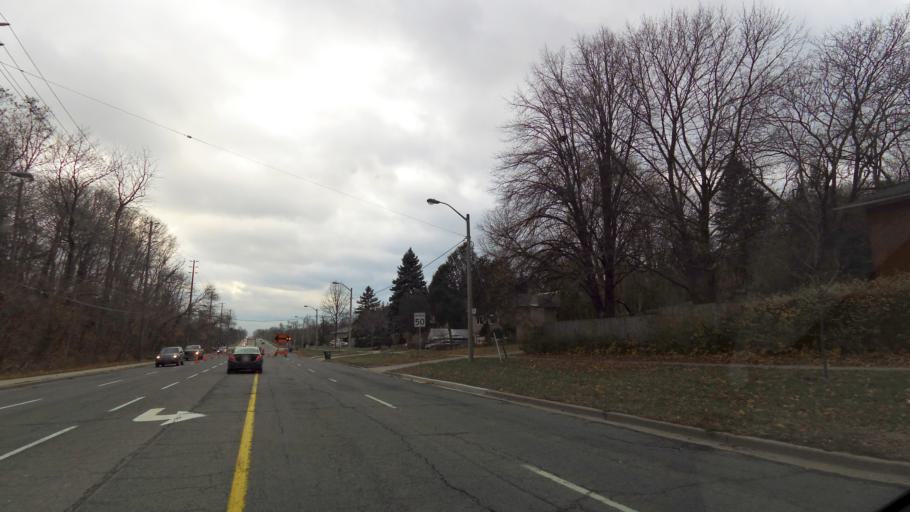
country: CA
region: Ontario
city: Etobicoke
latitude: 43.7339
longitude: -79.5639
